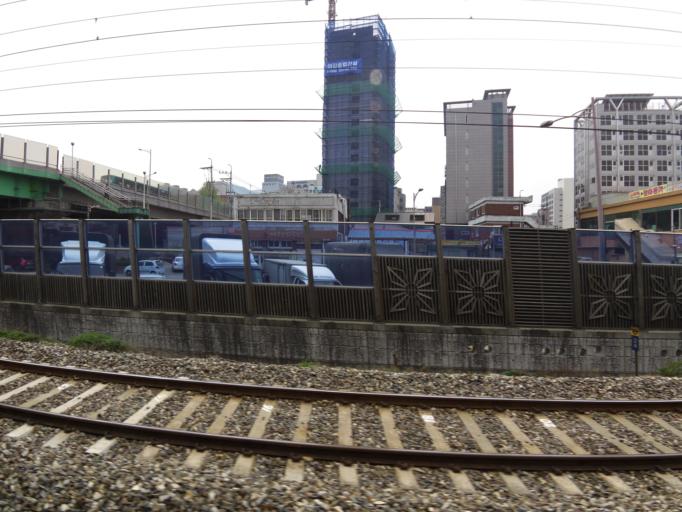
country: KR
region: Gyeonggi-do
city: Anyang-si
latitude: 37.3960
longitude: 126.9280
